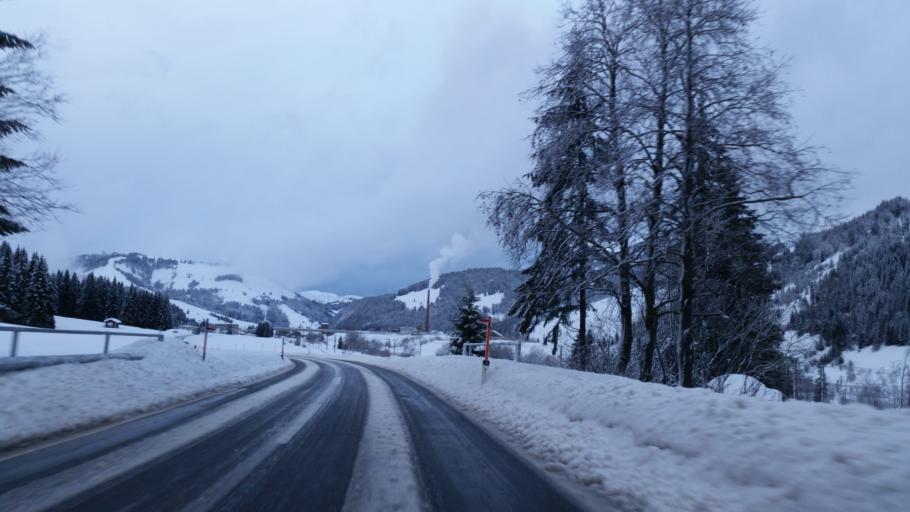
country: AT
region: Tyrol
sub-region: Politischer Bezirk Kitzbuhel
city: Hochfilzen
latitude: 47.4568
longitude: 12.6429
